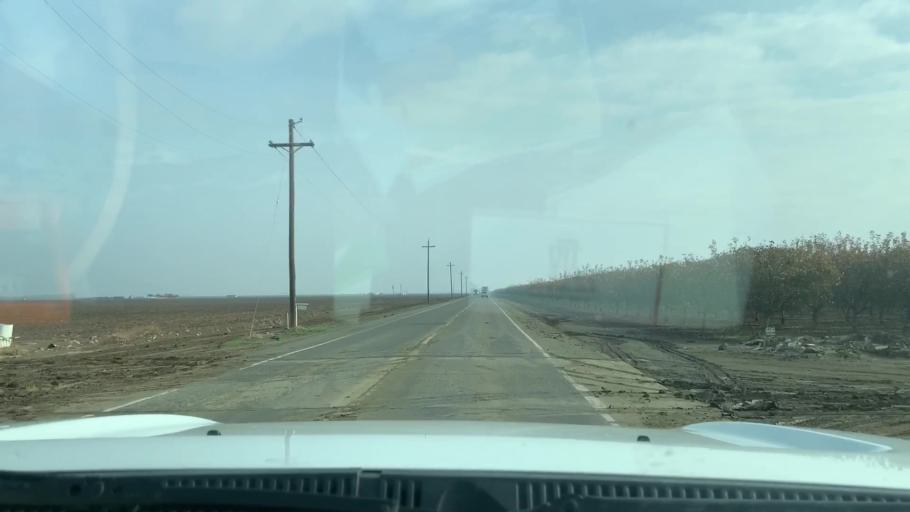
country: US
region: California
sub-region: Kings County
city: Lemoore Station
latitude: 36.2554
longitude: -119.9768
